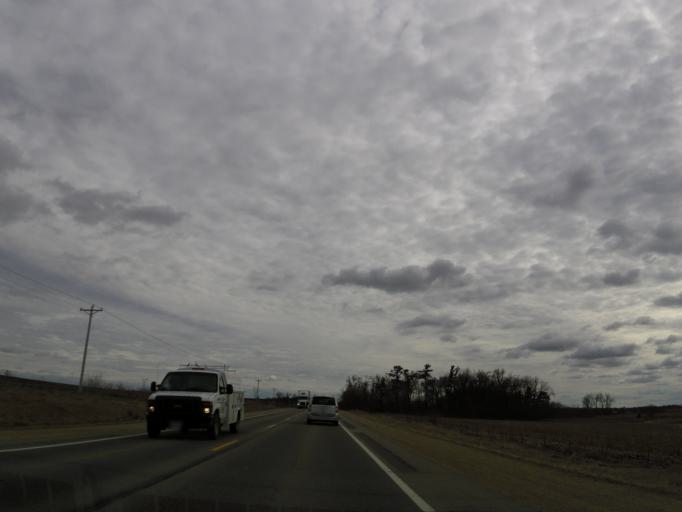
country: US
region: Iowa
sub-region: Chickasaw County
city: New Hampton
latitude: 43.1178
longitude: -92.2980
